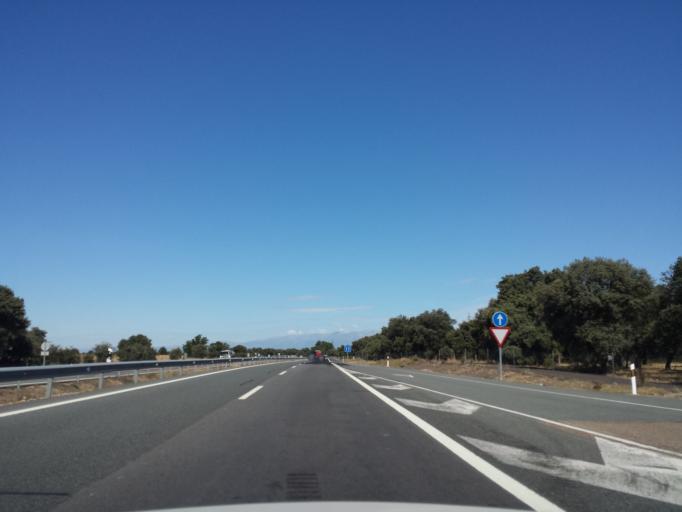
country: ES
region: Castille-La Mancha
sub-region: Province of Toledo
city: Alcanizo
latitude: 39.9203
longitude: -5.0833
